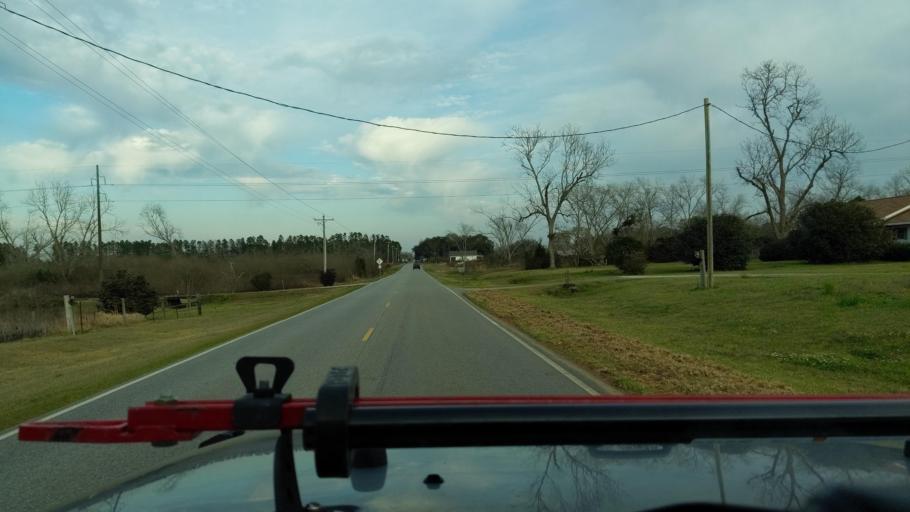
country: US
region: Alabama
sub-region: Baldwin County
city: Foley
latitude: 30.4579
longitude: -87.7476
